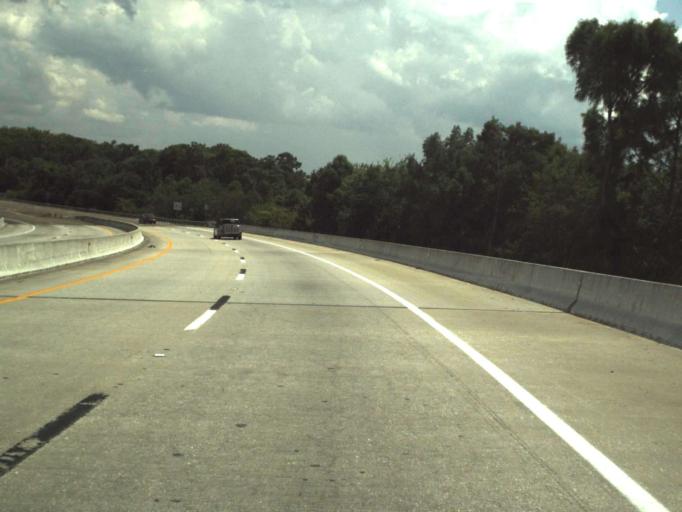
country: US
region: Florida
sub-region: Volusia County
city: DeBary
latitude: 28.8363
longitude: -81.3248
